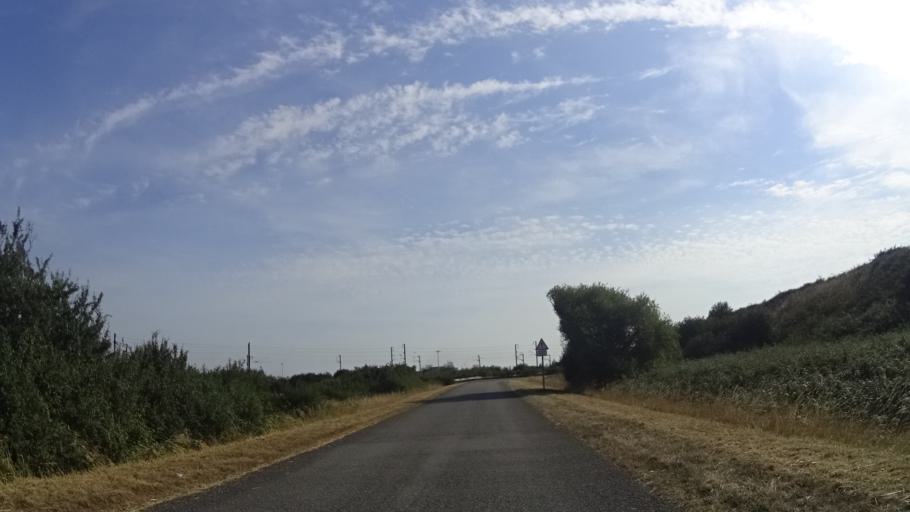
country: FR
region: Pays de la Loire
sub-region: Departement de la Loire-Atlantique
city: Donges
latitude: 47.3250
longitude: -2.1087
